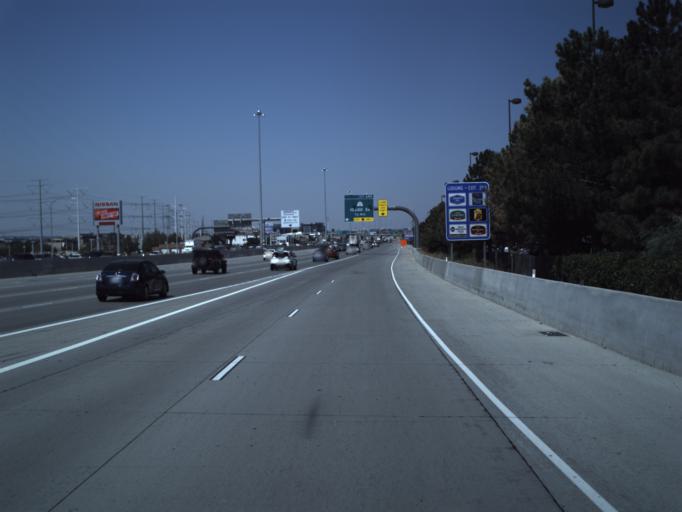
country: US
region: Utah
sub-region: Salt Lake County
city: White City
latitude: 40.5478
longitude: -111.8952
